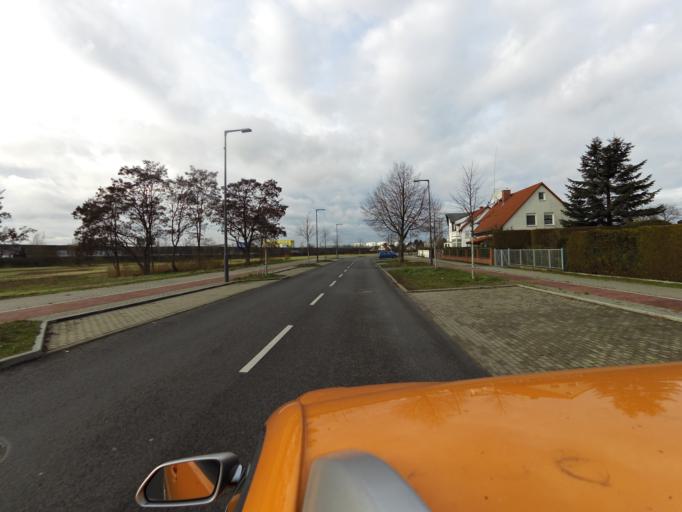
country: DE
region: Berlin
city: Johannisthal
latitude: 52.4298
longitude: 13.5106
